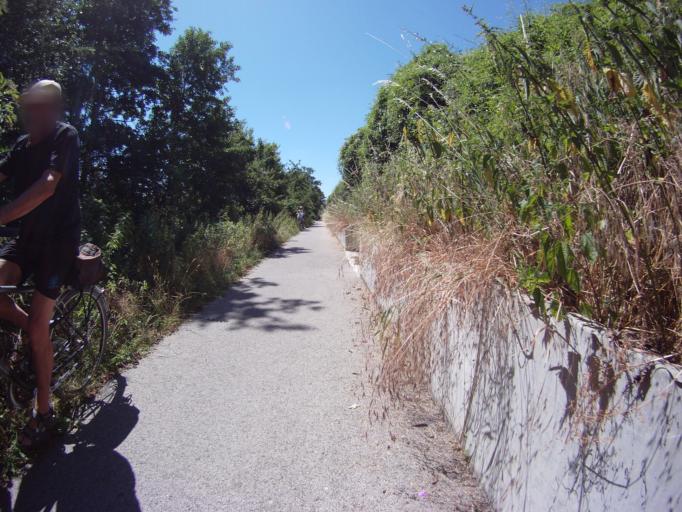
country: FR
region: Champagne-Ardenne
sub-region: Departement de la Marne
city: Mardeuil
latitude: 49.0725
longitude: 3.9365
